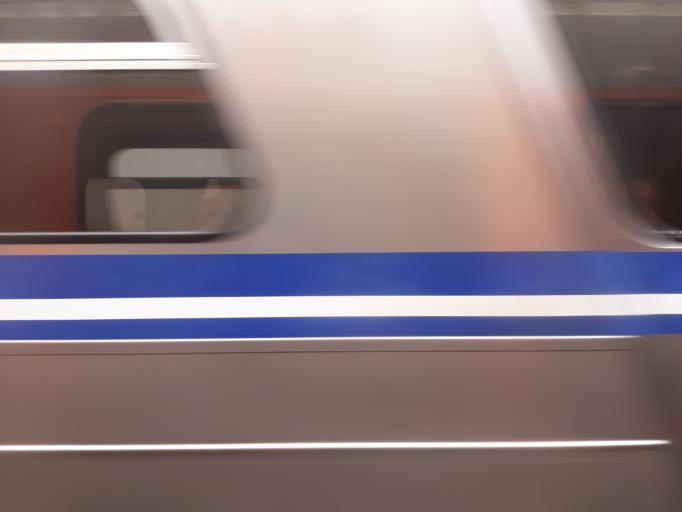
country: TW
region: Taiwan
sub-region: Yilan
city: Yilan
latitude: 24.6924
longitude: 121.7751
